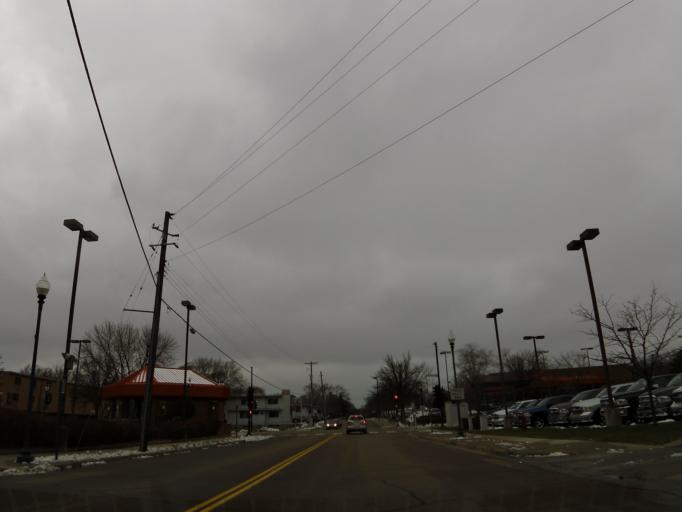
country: US
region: Minnesota
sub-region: Hennepin County
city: Minnetonka Mills
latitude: 44.9238
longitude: -93.4063
